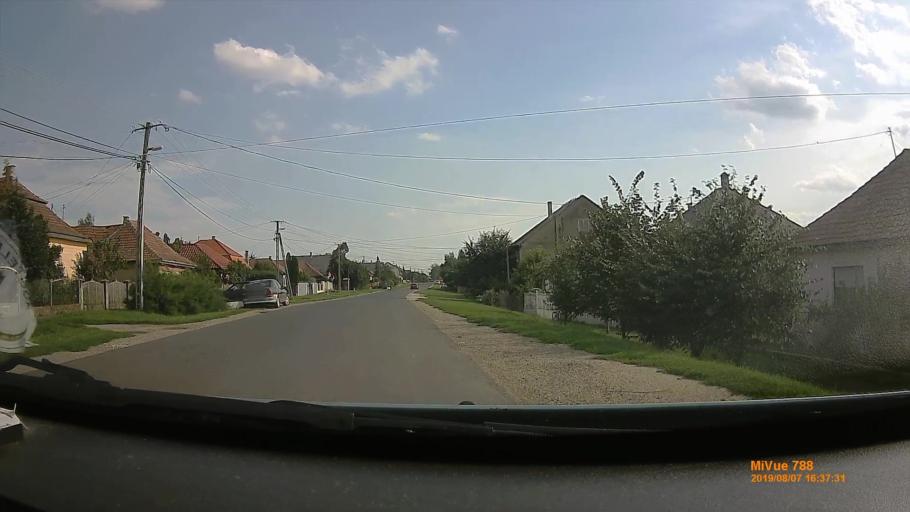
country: HU
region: Borsod-Abauj-Zemplen
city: Gonc
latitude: 48.4115
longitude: 21.2303
